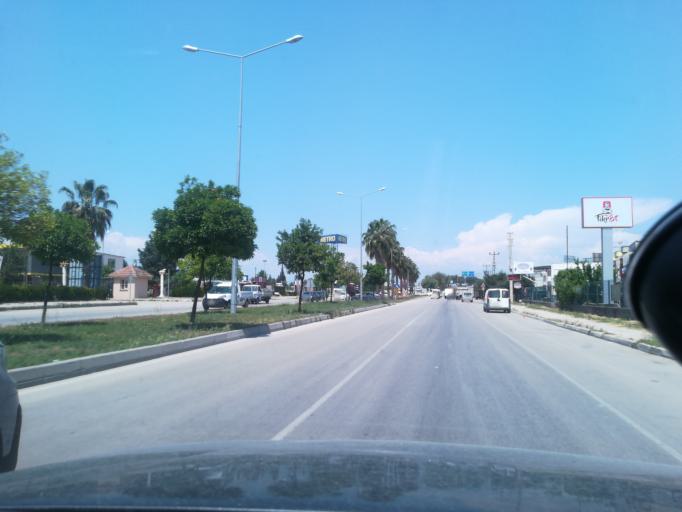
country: TR
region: Adana
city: Seyhan
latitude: 36.9931
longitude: 35.2525
